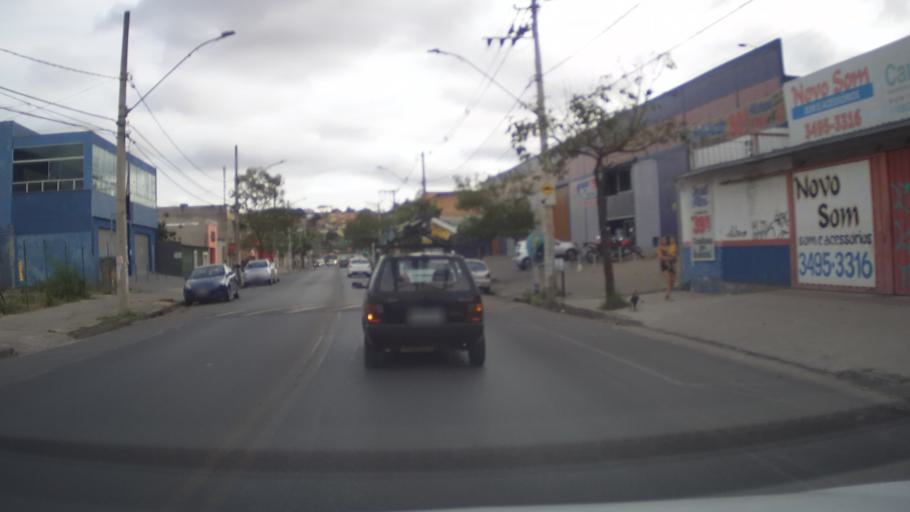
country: BR
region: Minas Gerais
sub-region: Belo Horizonte
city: Belo Horizonte
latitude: -19.8293
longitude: -43.9708
